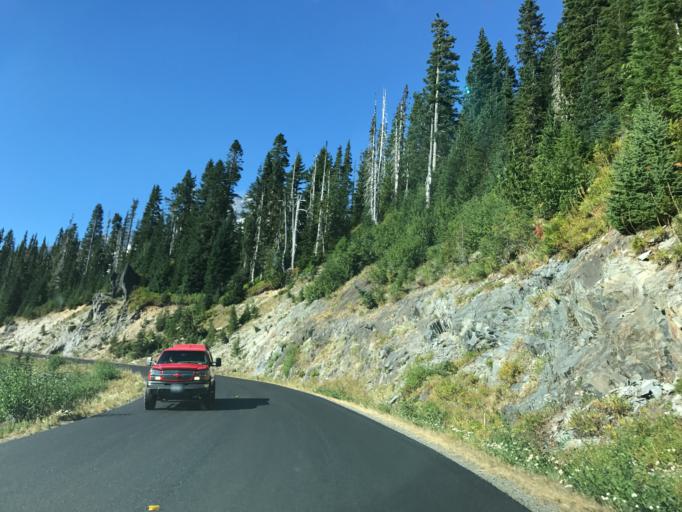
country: US
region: Washington
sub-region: Pierce County
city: Buckley
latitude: 46.7806
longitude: -121.7474
